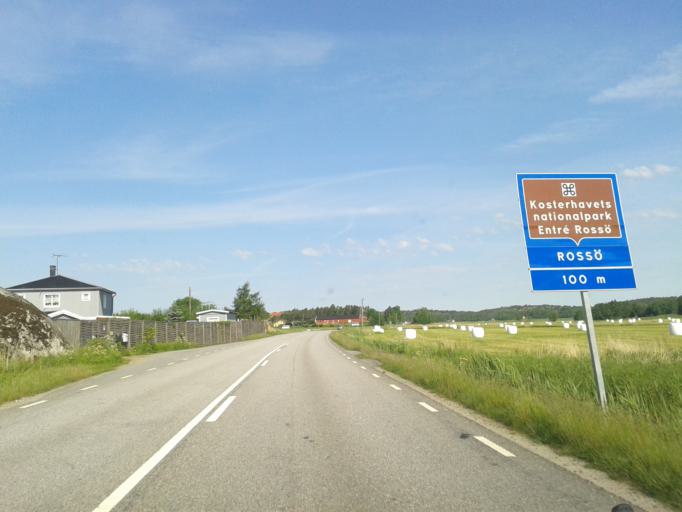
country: SE
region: Vaestra Goetaland
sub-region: Stromstads Kommun
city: Stroemstad
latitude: 58.8605
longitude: 11.2531
